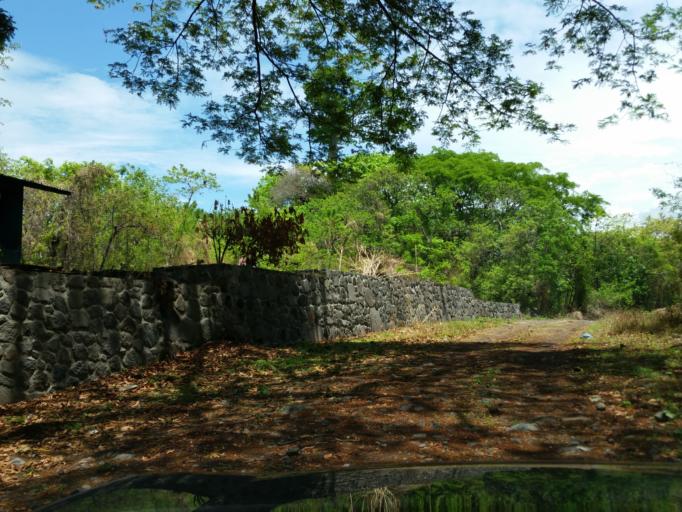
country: NI
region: Granada
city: Granada
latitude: 11.9090
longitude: -85.9103
